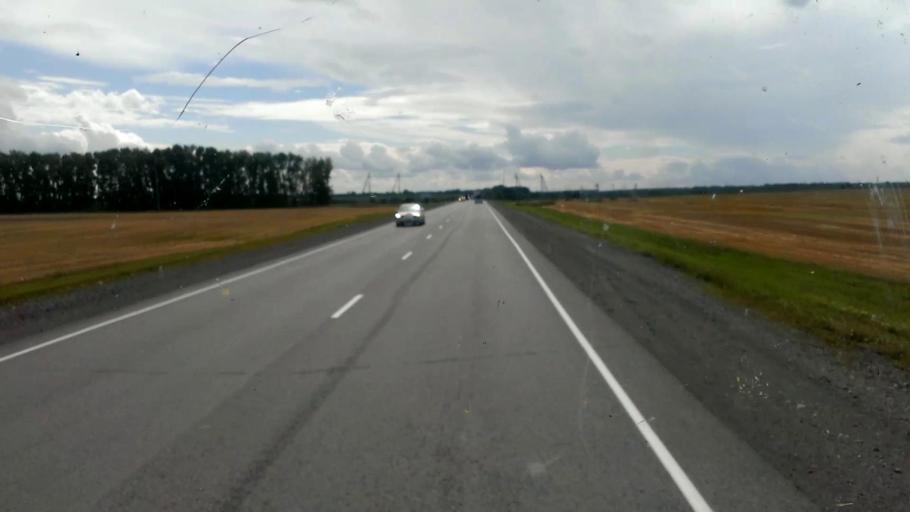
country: RU
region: Altai Krai
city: Zonal'noye
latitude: 52.7859
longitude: 84.8992
